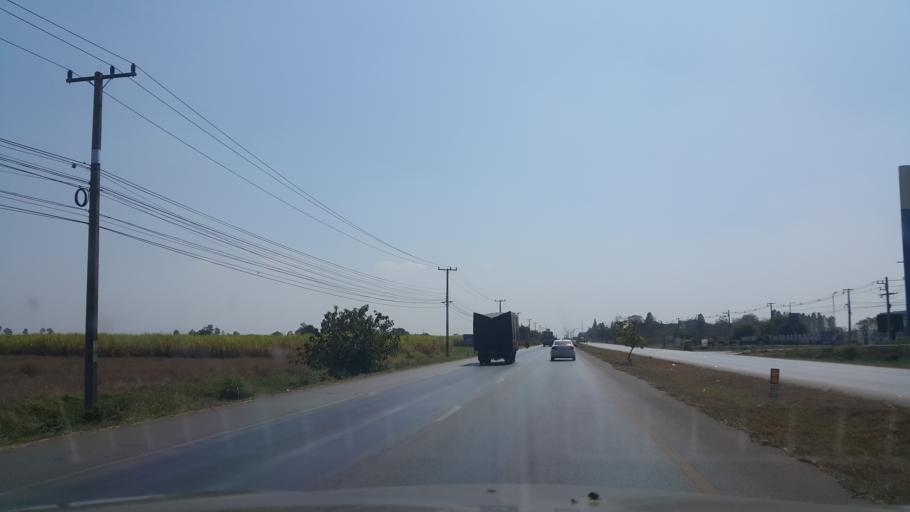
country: TH
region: Changwat Udon Thani
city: Non Sa-at
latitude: 16.9997
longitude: 102.8933
